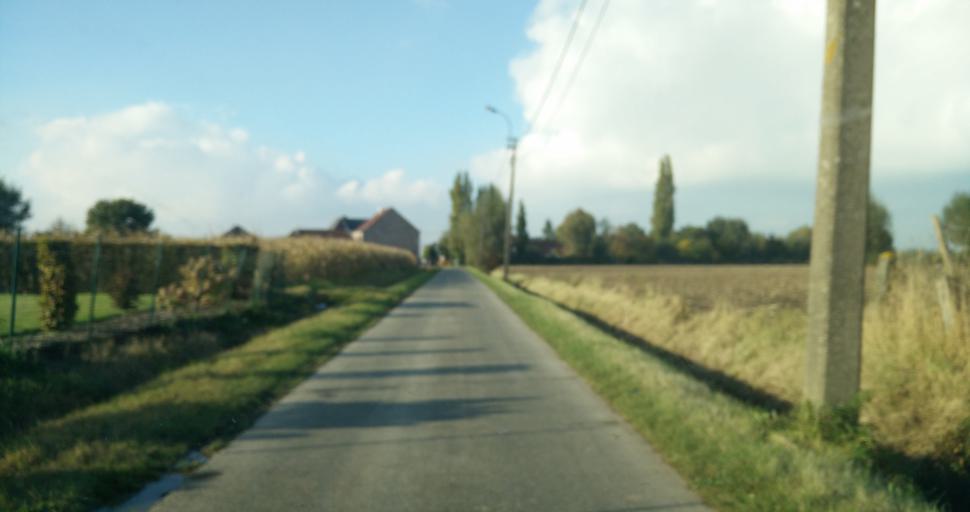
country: BE
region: Flanders
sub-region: Provincie Oost-Vlaanderen
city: Oosterzele
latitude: 50.9121
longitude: 3.7826
